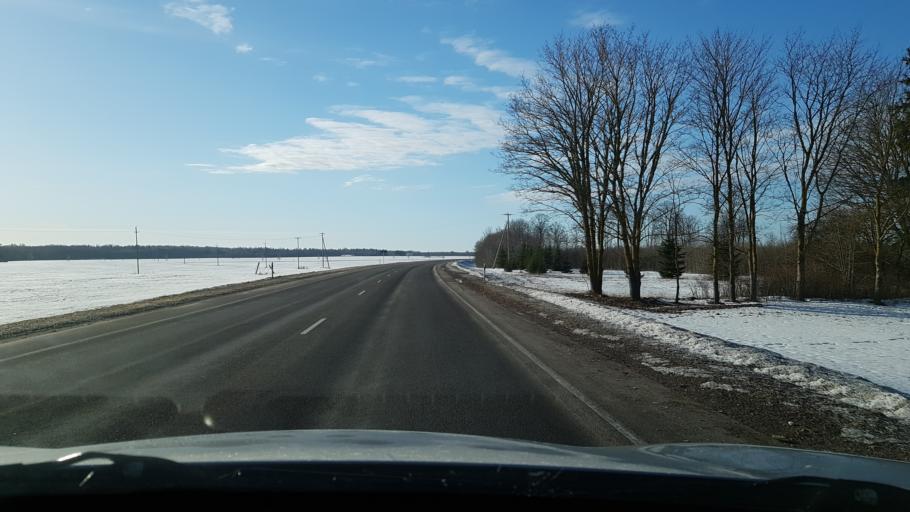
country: EE
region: Jogevamaa
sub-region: Poltsamaa linn
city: Poltsamaa
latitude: 58.7268
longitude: 25.7646
